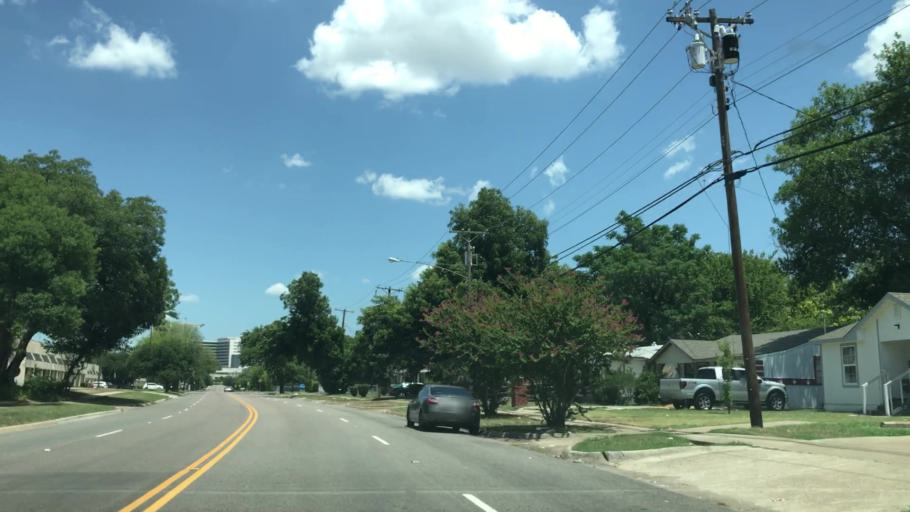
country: US
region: Texas
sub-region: Dallas County
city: Dallas
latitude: 32.8151
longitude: -96.8633
